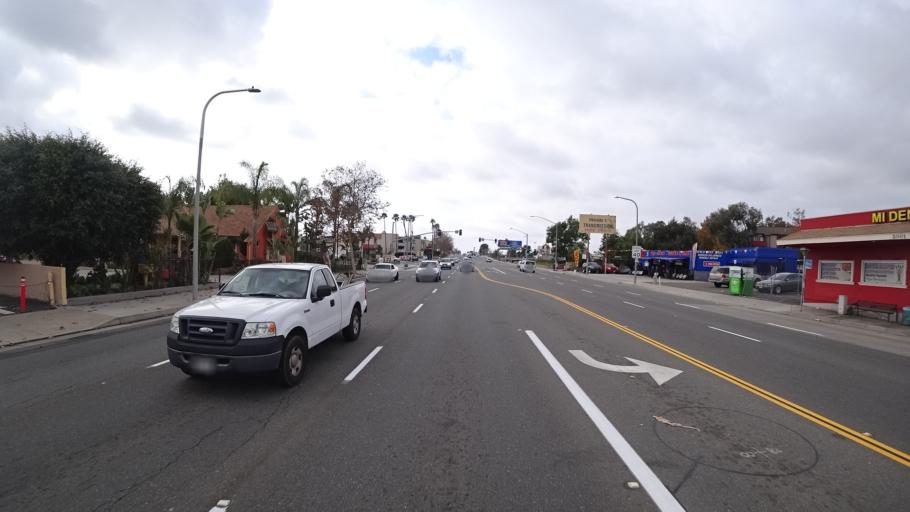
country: US
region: California
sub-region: Orange County
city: Santa Ana
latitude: 33.7599
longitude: -117.8970
